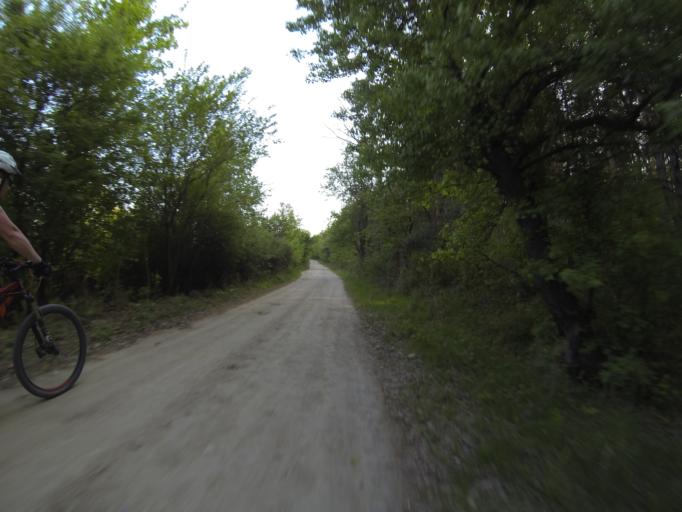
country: RO
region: Dolj
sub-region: Comuna Filiasi
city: Fratostita
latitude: 44.5617
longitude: 23.5856
